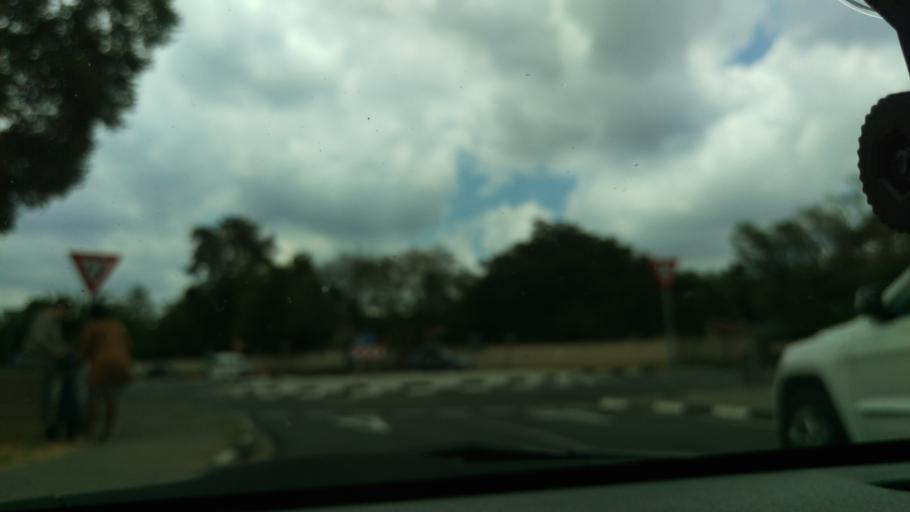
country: ZA
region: Gauteng
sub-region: City of Johannesburg Metropolitan Municipality
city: Midrand
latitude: -26.0393
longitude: 28.0459
